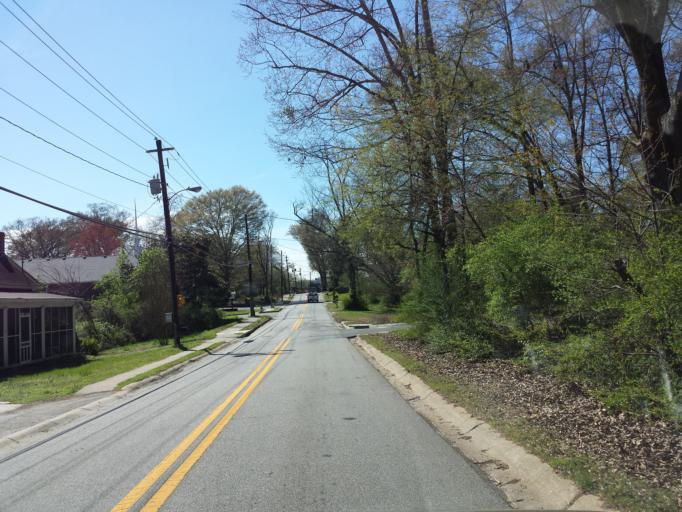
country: US
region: Georgia
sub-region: Cobb County
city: Smyrna
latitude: 33.8838
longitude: -84.5099
